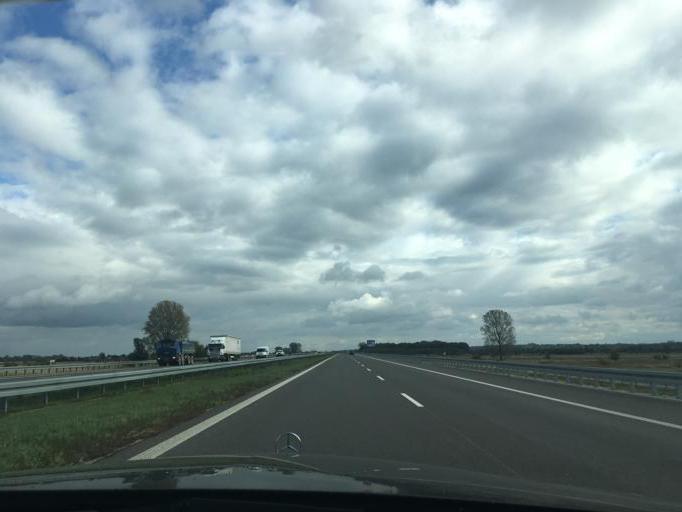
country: PL
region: Subcarpathian Voivodeship
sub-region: Powiat rzeszowski
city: Wolka Podlesna
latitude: 50.0942
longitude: 22.1352
